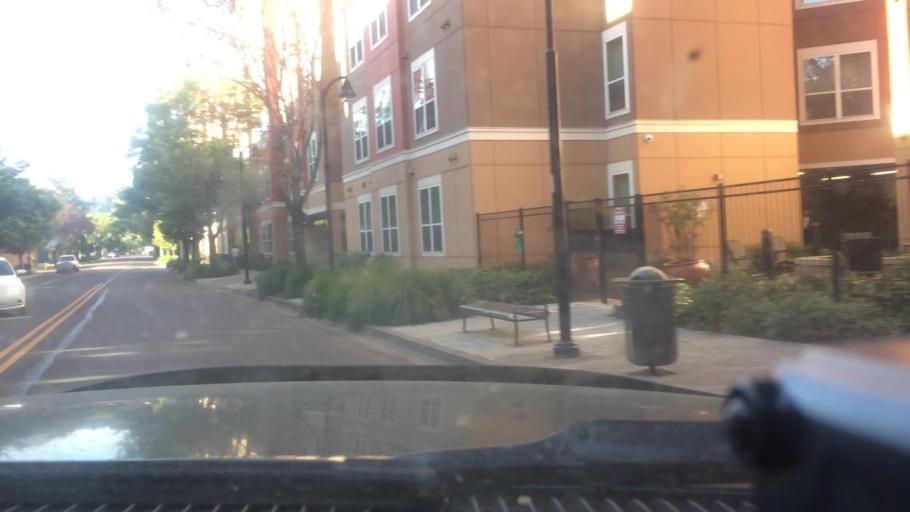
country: US
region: Oregon
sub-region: Lane County
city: Eugene
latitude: 44.0457
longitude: -123.0942
